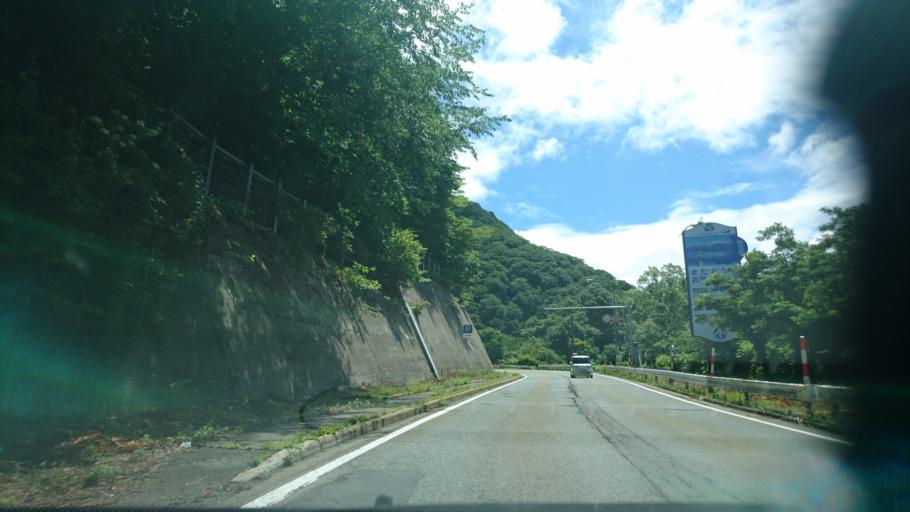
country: JP
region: Iwate
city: Shizukuishi
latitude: 39.6937
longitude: 140.7814
